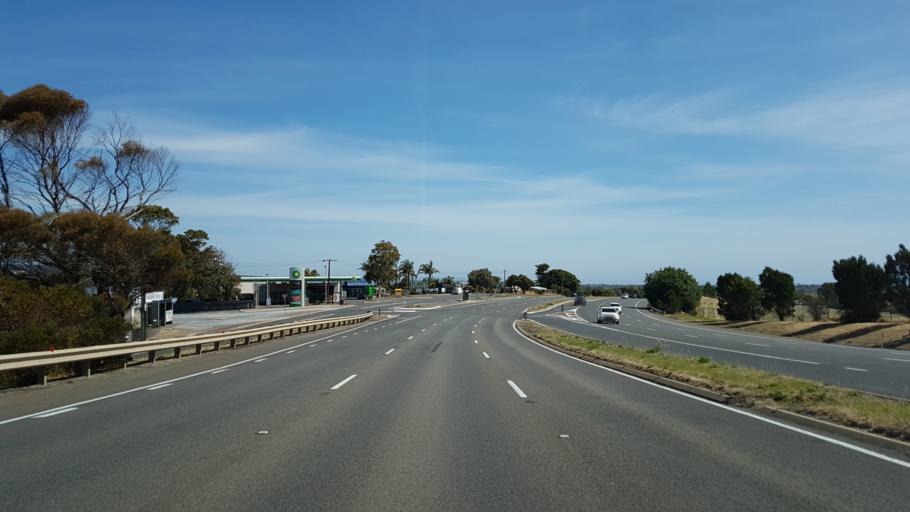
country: AU
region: South Australia
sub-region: Marion
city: Trott Park
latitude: -35.0697
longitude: 138.5545
